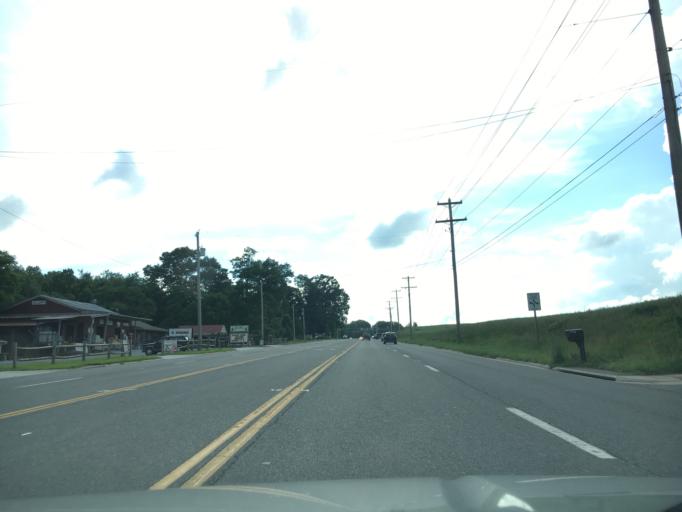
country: US
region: Virginia
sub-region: Bedford County
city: Forest
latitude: 37.3653
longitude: -79.2740
